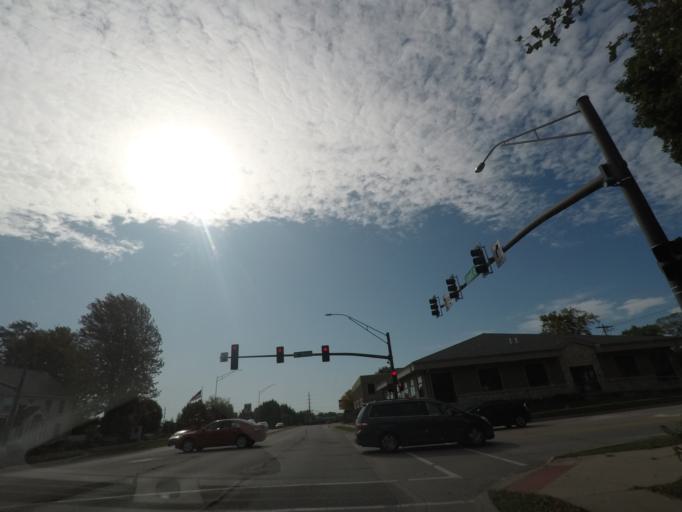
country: US
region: Iowa
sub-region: Story County
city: Ames
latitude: 42.0270
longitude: -93.6204
